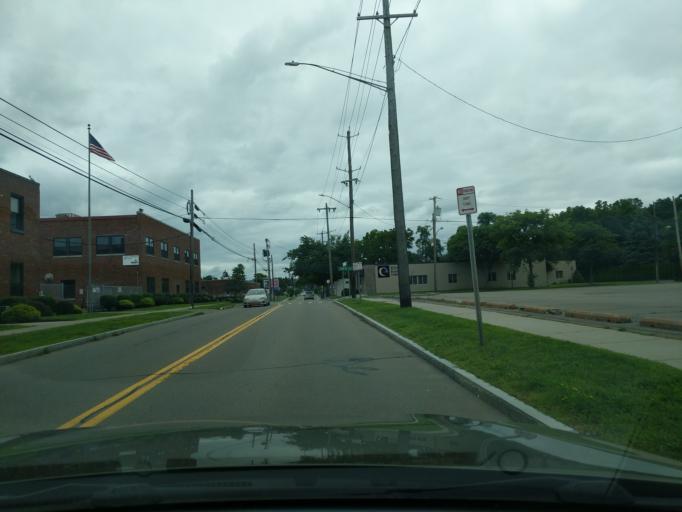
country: US
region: New York
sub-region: Chemung County
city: Elmira Heights
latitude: 42.1164
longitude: -76.8223
